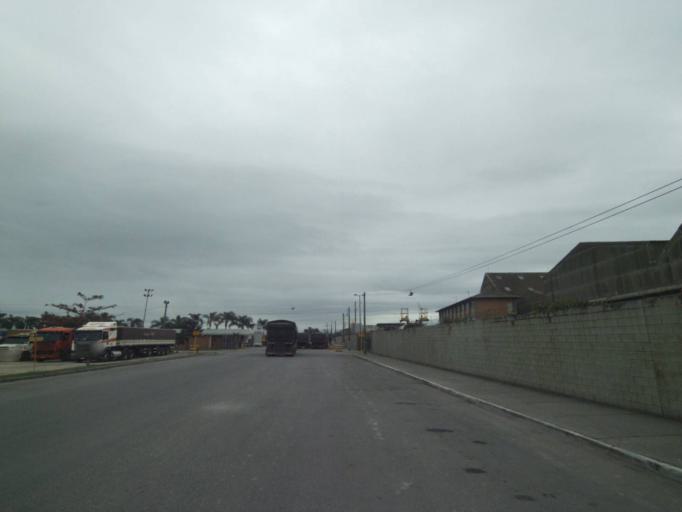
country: BR
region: Parana
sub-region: Paranagua
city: Paranagua
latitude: -25.5382
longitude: -48.5380
